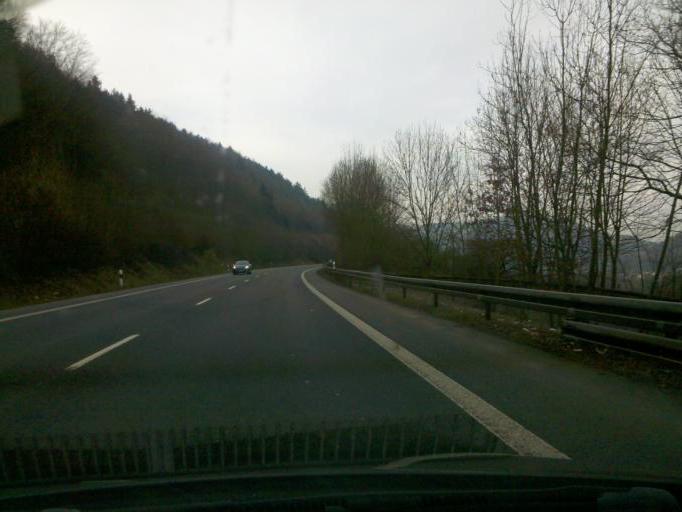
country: DE
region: Hesse
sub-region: Regierungsbezirk Giessen
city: Haiger
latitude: 50.7439
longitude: 8.2471
